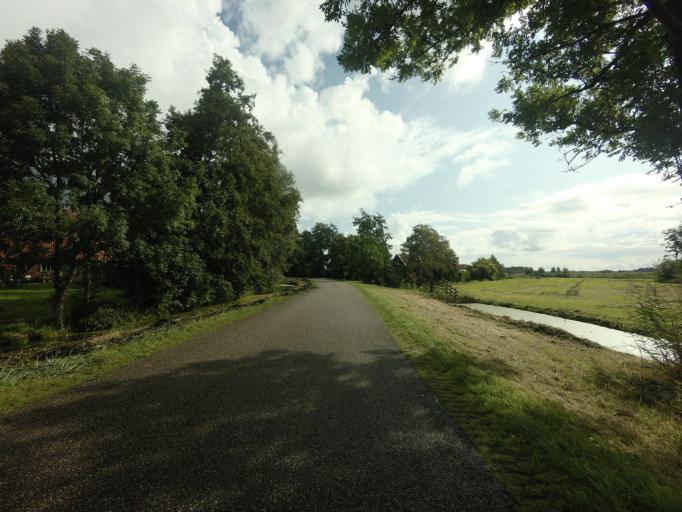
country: NL
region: Friesland
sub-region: Gemeente Tytsjerksteradiel
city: Garyp
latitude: 53.1511
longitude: 5.9445
